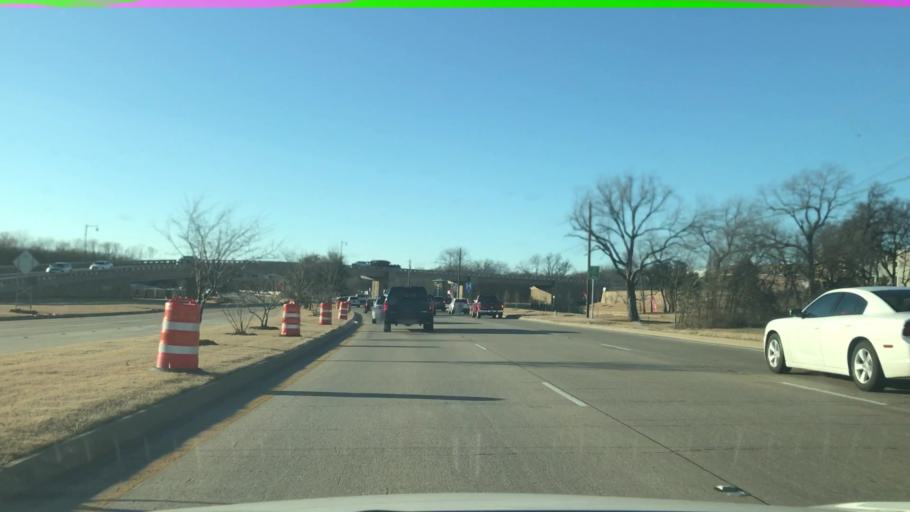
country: US
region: Texas
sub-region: Dallas County
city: Coppell
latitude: 32.9852
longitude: -97.0414
